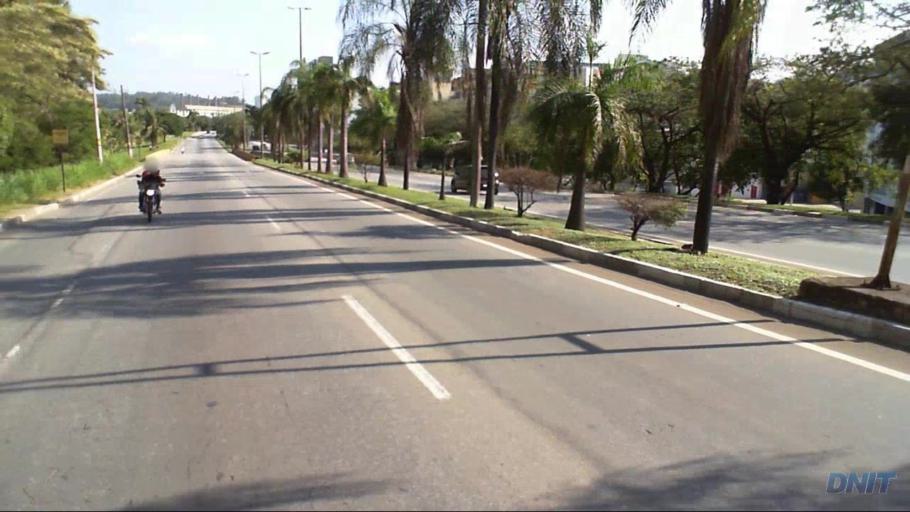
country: BR
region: Minas Gerais
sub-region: Ipatinga
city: Ipatinga
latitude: -19.4777
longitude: -42.5435
